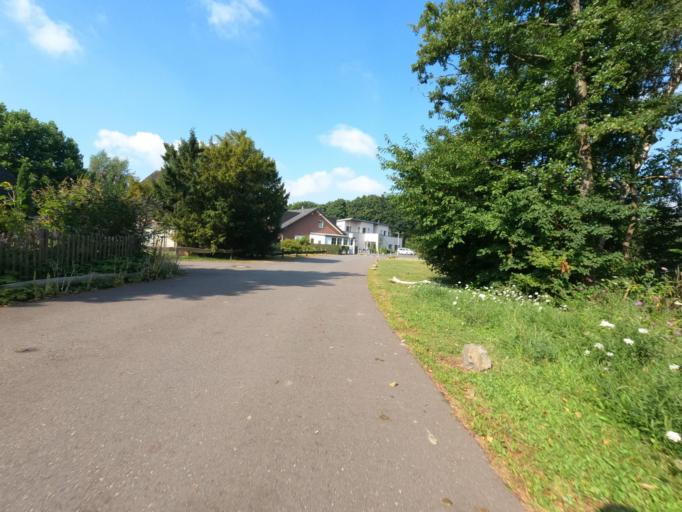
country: DE
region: North Rhine-Westphalia
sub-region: Regierungsbezirk Koln
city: Heinsberg
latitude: 51.0700
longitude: 6.0899
